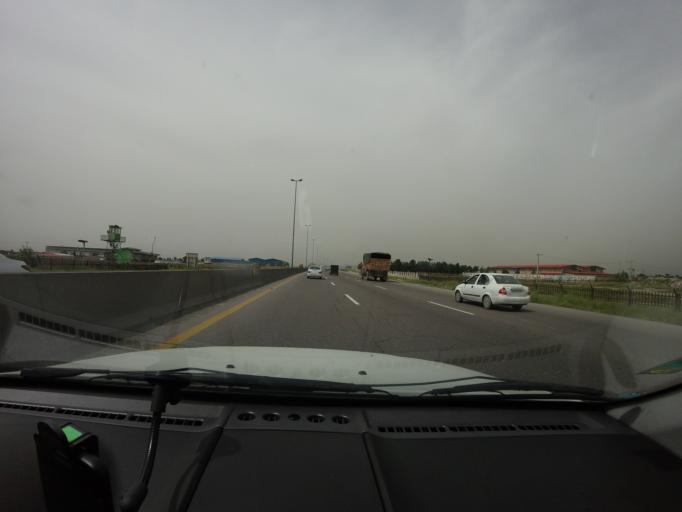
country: IR
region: Tehran
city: Robat Karim
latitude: 35.5431
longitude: 51.1159
